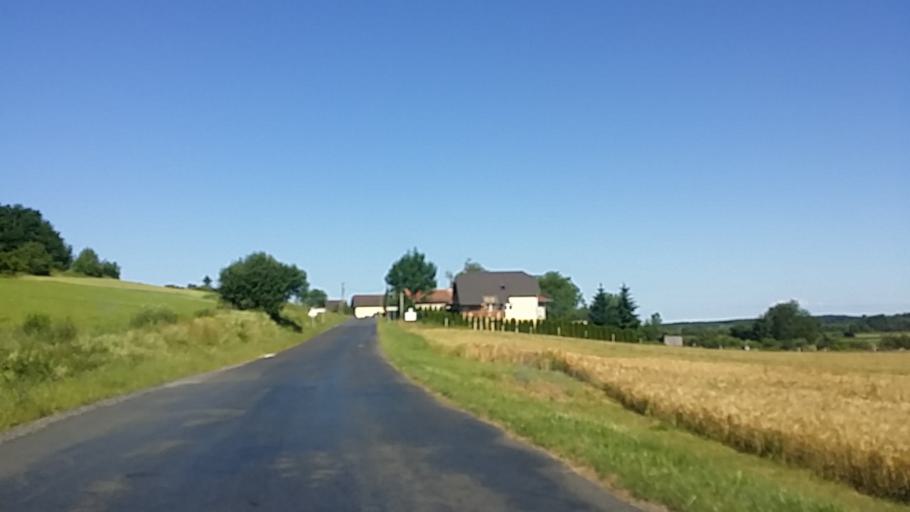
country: HU
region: Zala
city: Zalaegerszeg
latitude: 46.8679
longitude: 16.7484
